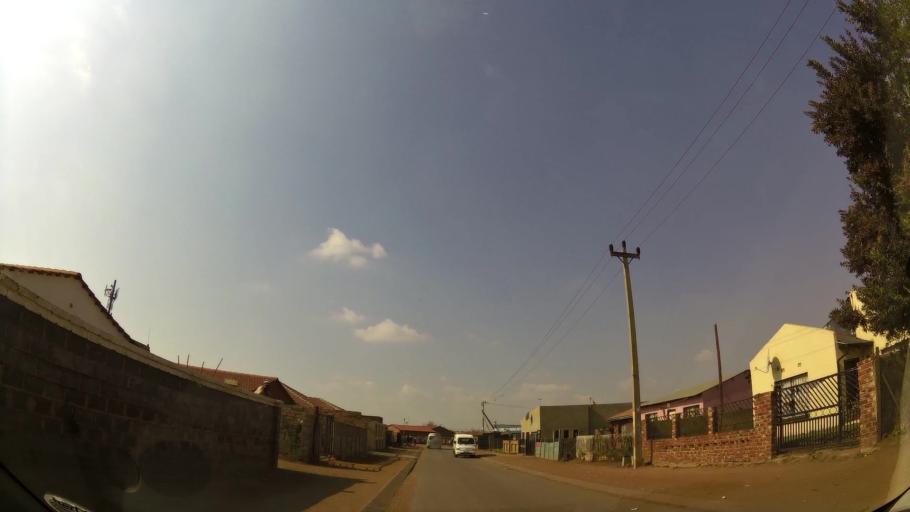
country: ZA
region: Gauteng
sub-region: Ekurhuleni Metropolitan Municipality
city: Springs
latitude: -26.1041
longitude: 28.4815
